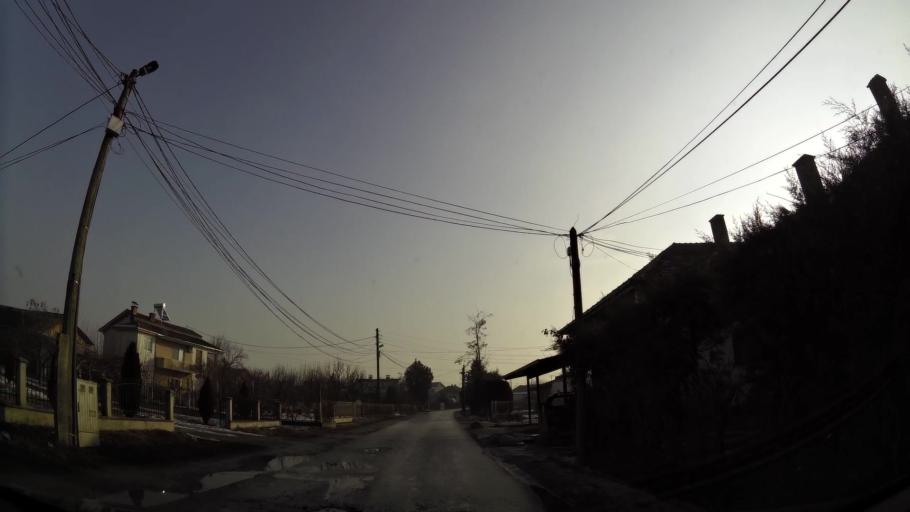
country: MK
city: Kadino
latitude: 41.9588
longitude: 21.6016
